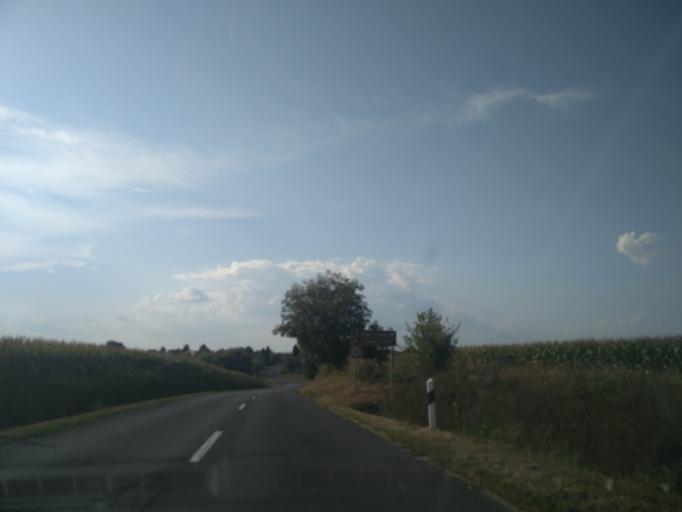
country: HU
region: Zala
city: Zalaegerszeg
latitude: 46.8670
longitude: 16.8307
